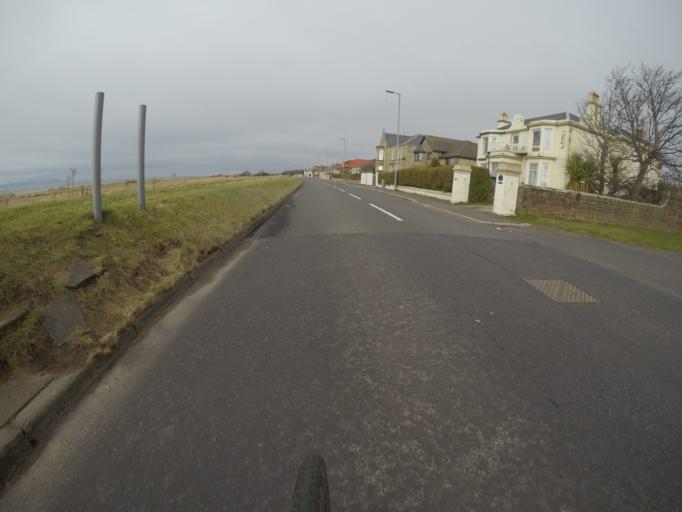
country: GB
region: Scotland
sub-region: North Ayrshire
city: Ardrossan
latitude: 55.6490
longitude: -4.8148
